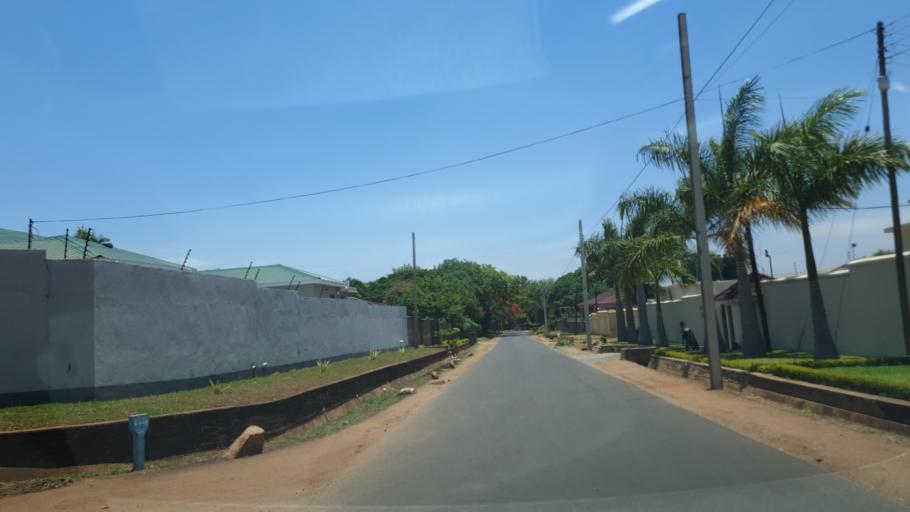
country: MW
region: Central Region
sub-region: Lilongwe District
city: Lilongwe
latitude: -13.9805
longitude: 33.7459
